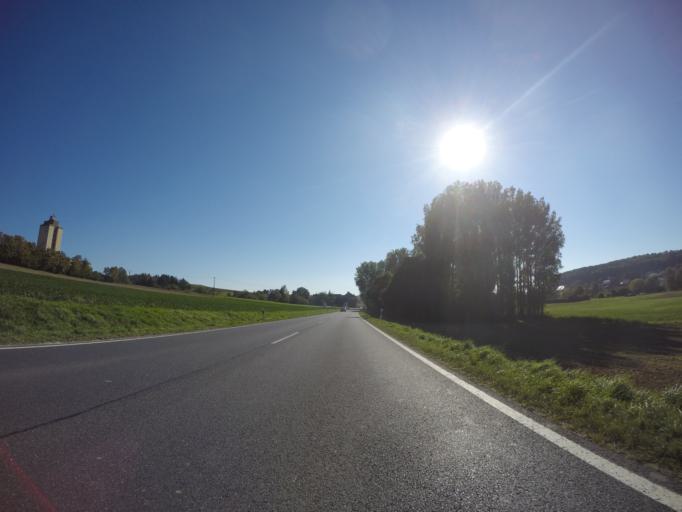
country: DE
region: Bavaria
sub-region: Regierungsbezirk Unterfranken
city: Greussenheim
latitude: 49.7996
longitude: 9.7540
